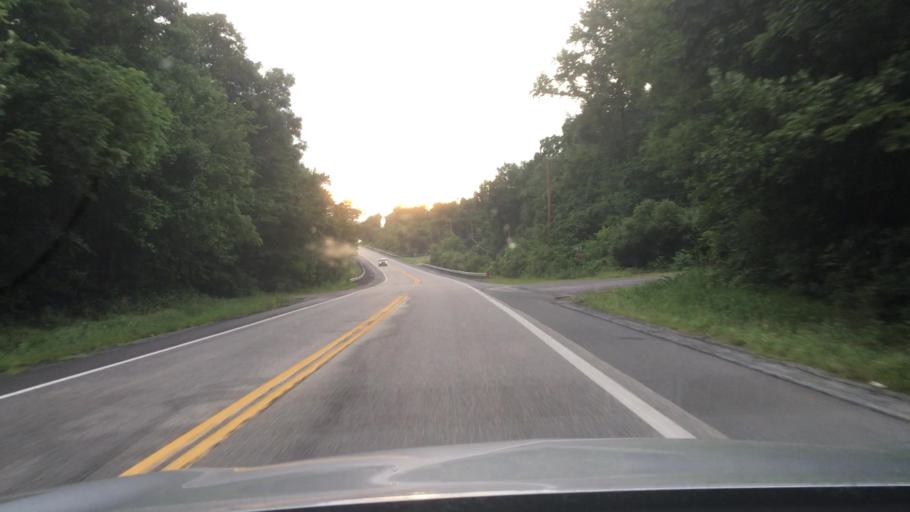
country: US
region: Pennsylvania
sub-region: York County
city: Dillsburg
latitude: 40.0943
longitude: -76.9589
